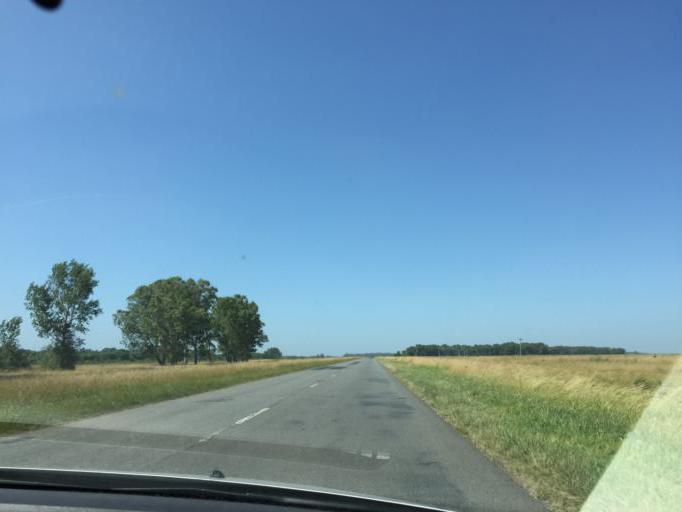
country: AR
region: Buenos Aires
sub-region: Partido de Rauch
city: Rauch
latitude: -36.6789
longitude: -59.0647
